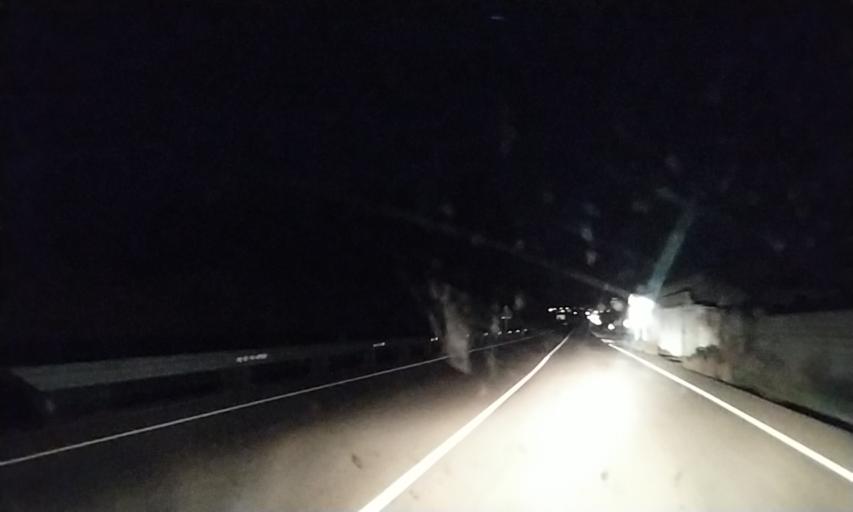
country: ES
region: Castille and Leon
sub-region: Provincia de Salamanca
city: Ciudad Rodrigo
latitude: 40.5797
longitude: -6.5375
